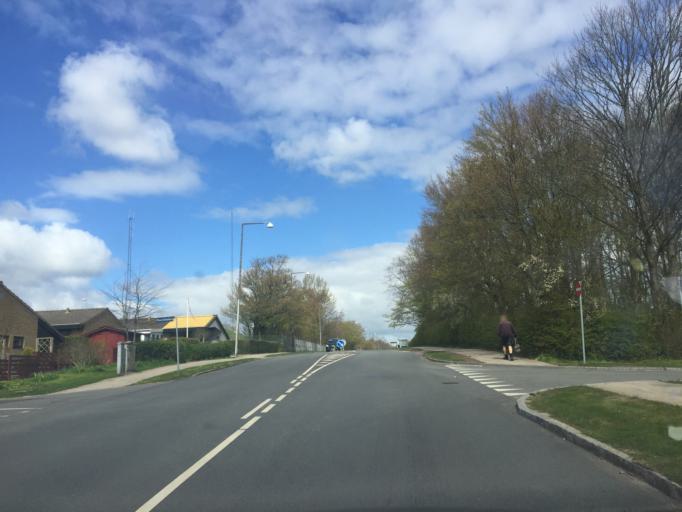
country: DK
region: South Denmark
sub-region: Odense Kommune
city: Bellinge
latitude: 55.3900
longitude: 10.3297
